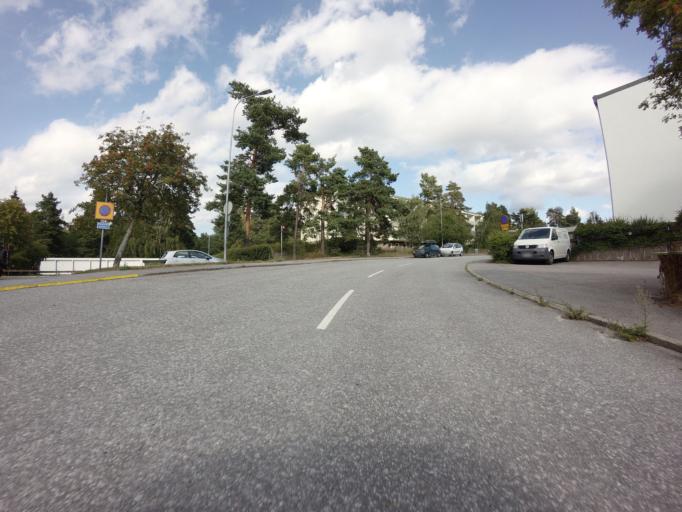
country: SE
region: Stockholm
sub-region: Lidingo
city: Lidingoe
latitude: 59.3751
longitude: 18.1390
